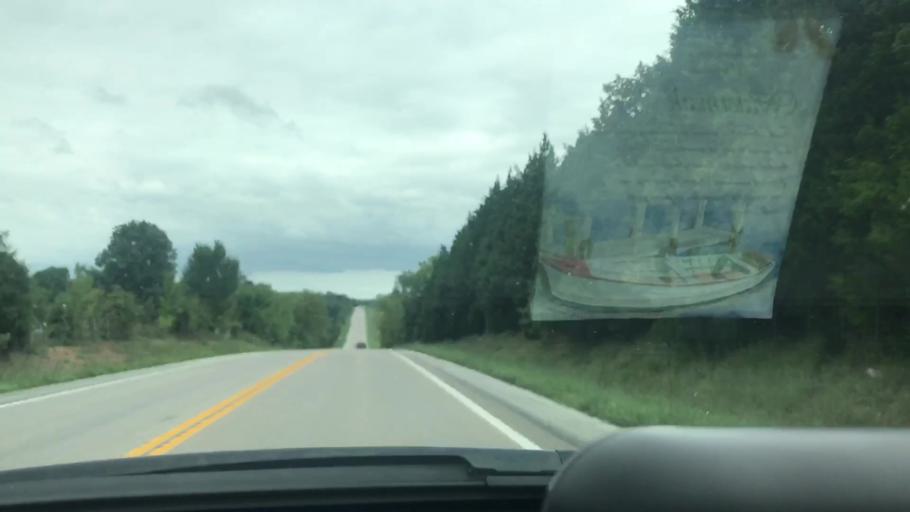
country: US
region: Missouri
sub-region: Dallas County
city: Buffalo
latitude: 37.7151
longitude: -93.1181
